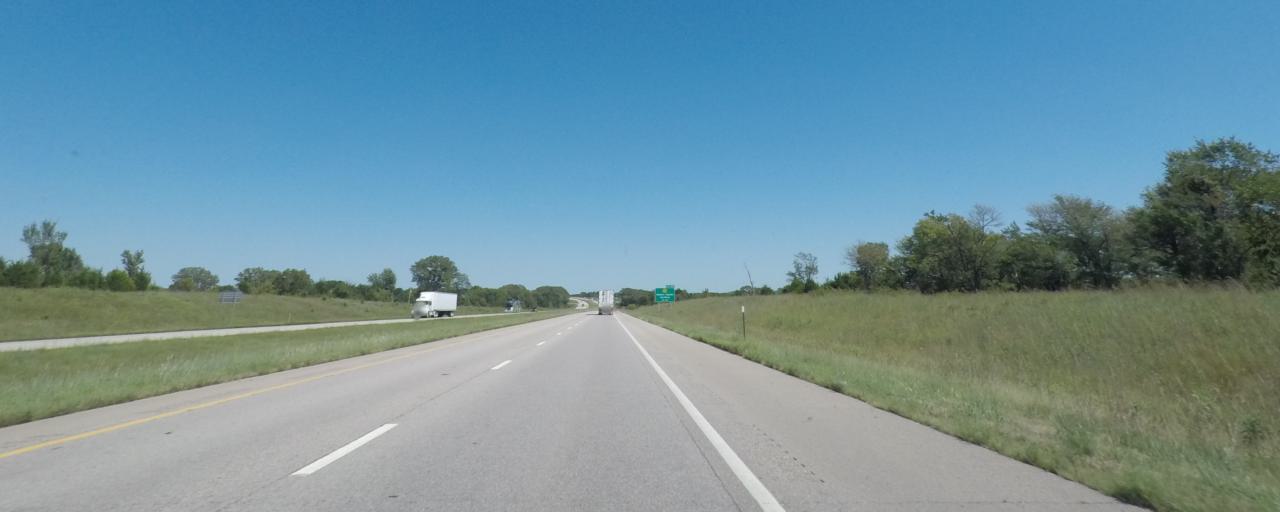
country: US
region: Kansas
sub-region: Lyon County
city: Emporia
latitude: 38.4091
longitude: -96.0031
